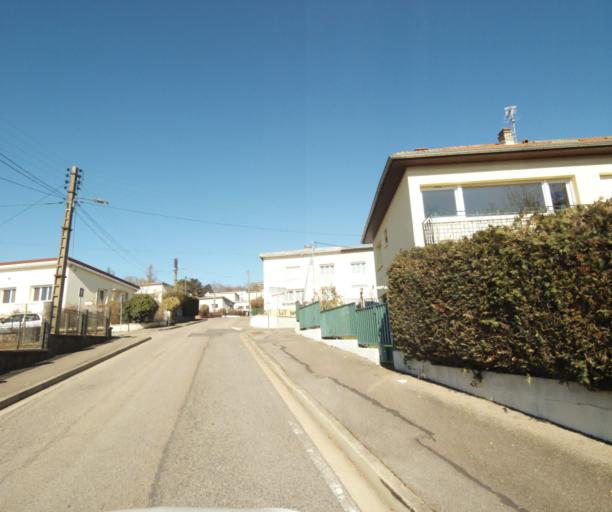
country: FR
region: Lorraine
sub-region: Departement de Meurthe-et-Moselle
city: Saint-Max
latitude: 48.7058
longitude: 6.1985
